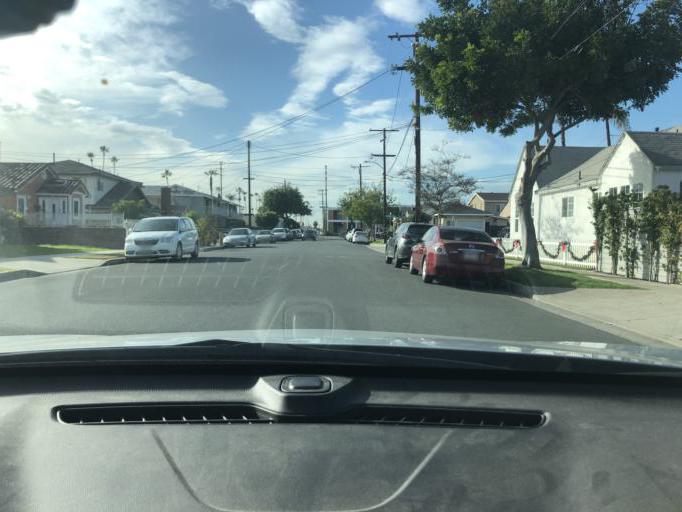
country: US
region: California
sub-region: Los Angeles County
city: Gardena
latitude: 33.8774
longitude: -118.3074
